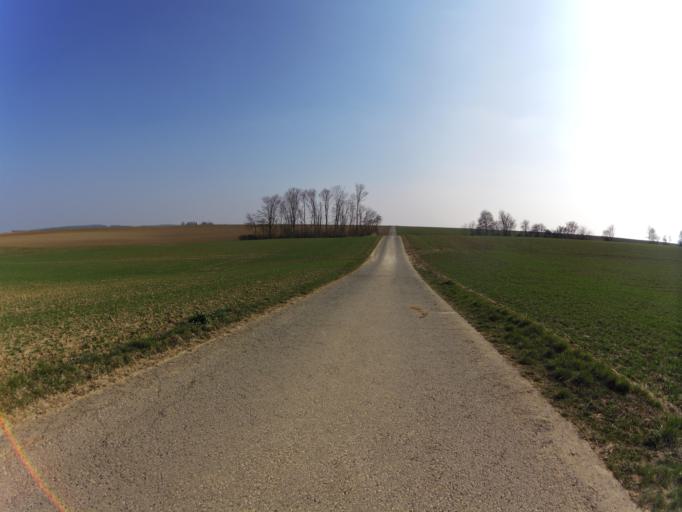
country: DE
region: Bavaria
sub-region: Regierungsbezirk Unterfranken
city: Gaukonigshofen
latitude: 49.6547
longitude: 9.9895
